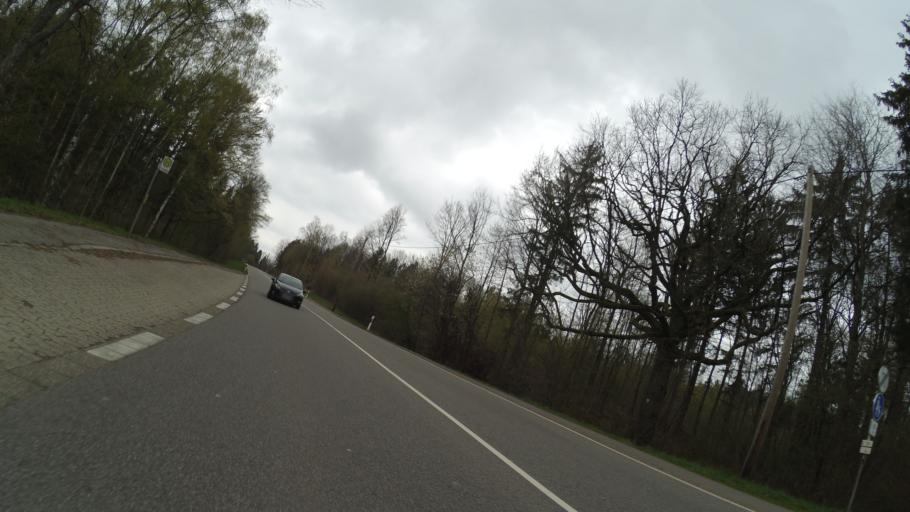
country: DE
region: Saarland
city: Merchweiler
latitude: 49.3529
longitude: 7.0760
